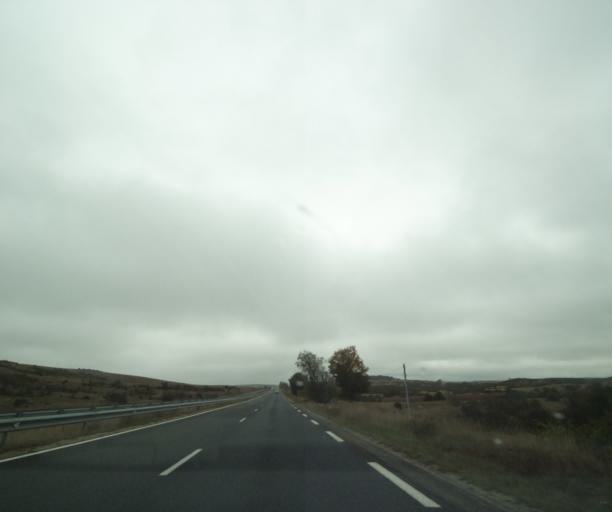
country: FR
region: Midi-Pyrenees
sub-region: Departement de l'Aveyron
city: La Cavalerie
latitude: 44.0532
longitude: 3.1295
